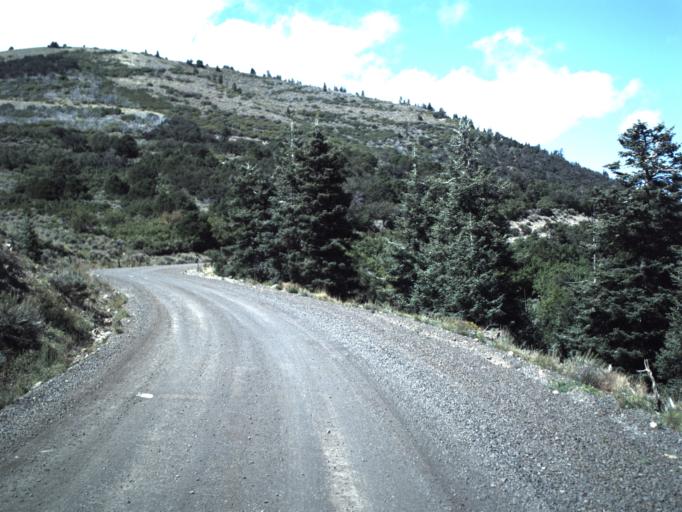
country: US
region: Utah
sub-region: Piute County
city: Junction
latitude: 38.2545
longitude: -112.3149
